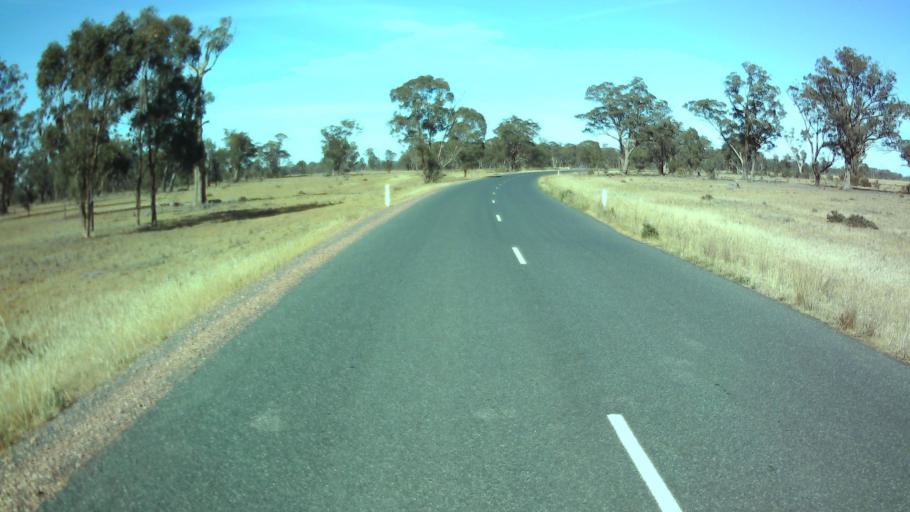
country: AU
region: New South Wales
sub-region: Weddin
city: Grenfell
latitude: -34.1120
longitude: 147.8491
